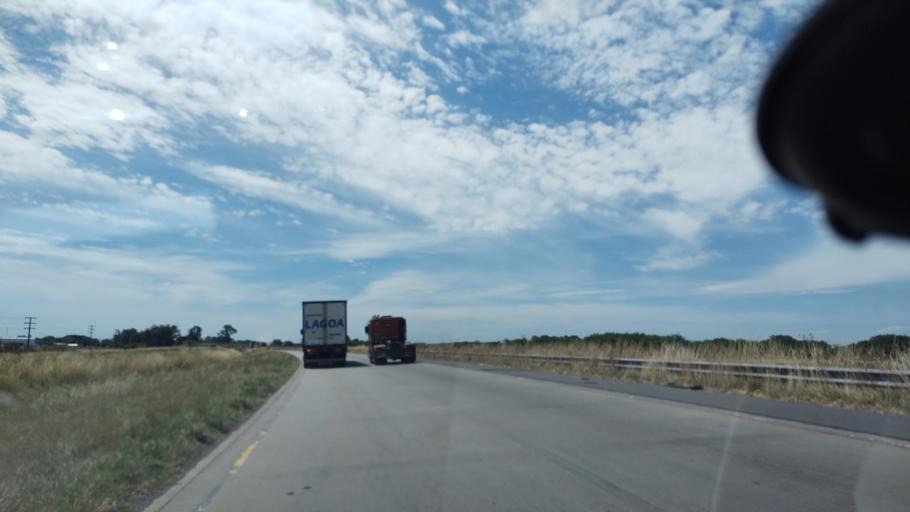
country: AR
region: Buenos Aires
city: Canuelas
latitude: -35.0454
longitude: -58.7112
